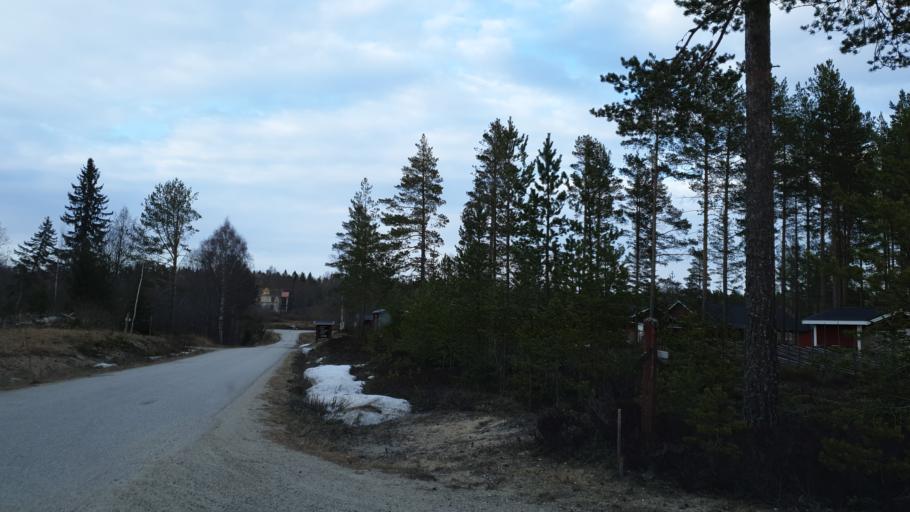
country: SE
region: Vaesternorrland
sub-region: Sundsvalls Kommun
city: Njurundabommen
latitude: 62.0328
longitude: 17.4151
